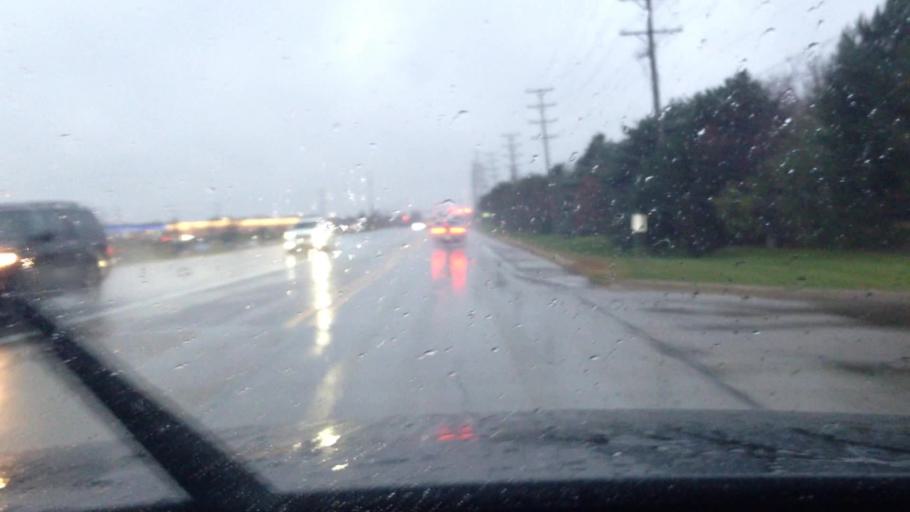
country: US
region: Illinois
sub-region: McHenry County
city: Huntley
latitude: 42.1796
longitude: -88.3838
